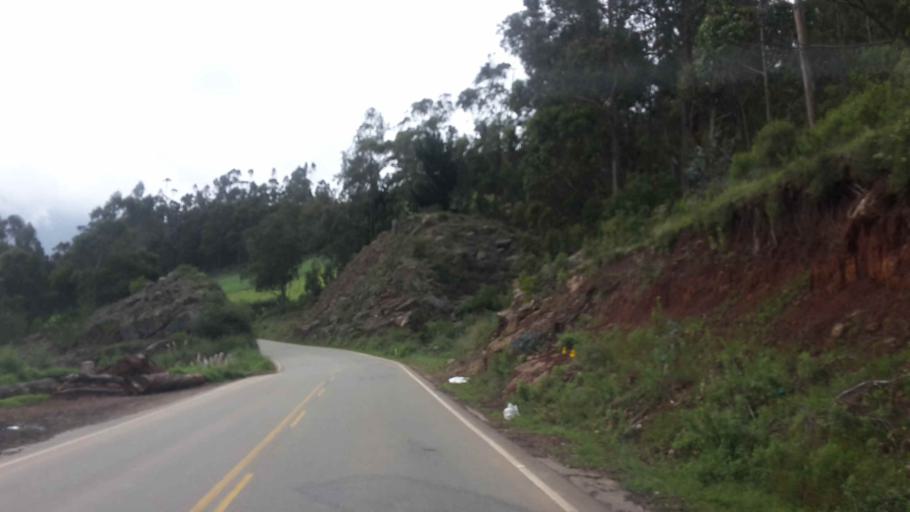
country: BO
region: Cochabamba
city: Totora
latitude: -17.5561
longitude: -65.3445
